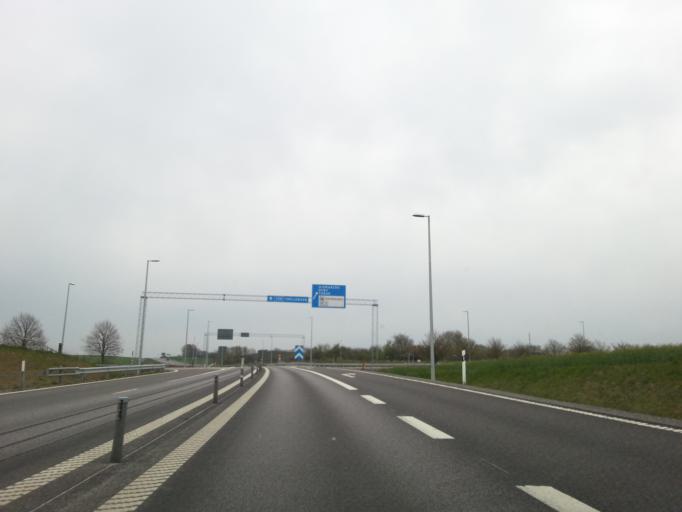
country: SE
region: Skane
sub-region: Svedala Kommun
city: Klagerup
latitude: 55.5794
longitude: 13.2521
